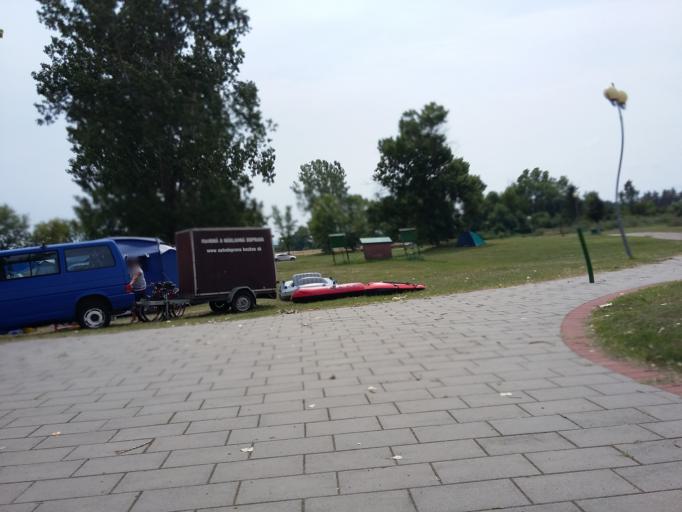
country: AT
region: Lower Austria
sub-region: Politischer Bezirk Ganserndorf
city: Drosing
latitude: 48.4905
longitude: 16.9549
